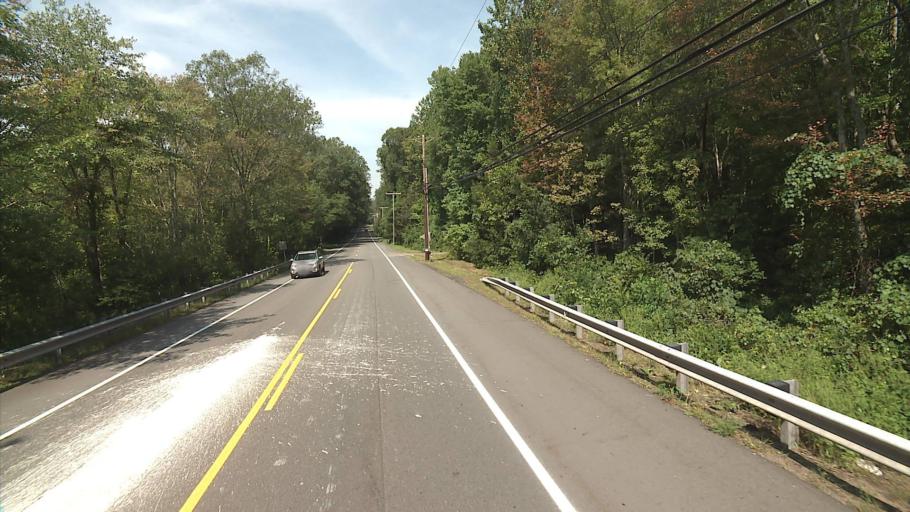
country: US
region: Connecticut
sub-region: New Haven County
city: Madison Center
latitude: 41.3257
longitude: -72.6174
